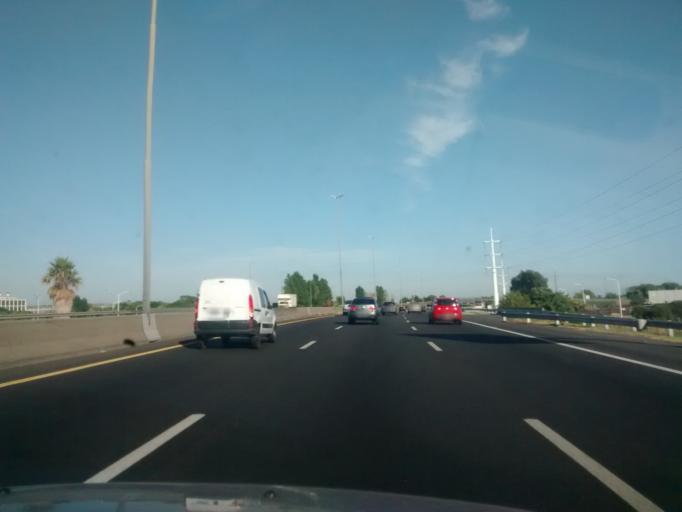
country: AR
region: Buenos Aires
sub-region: Partido de Quilmes
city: Quilmes
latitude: -34.7046
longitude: -58.2699
